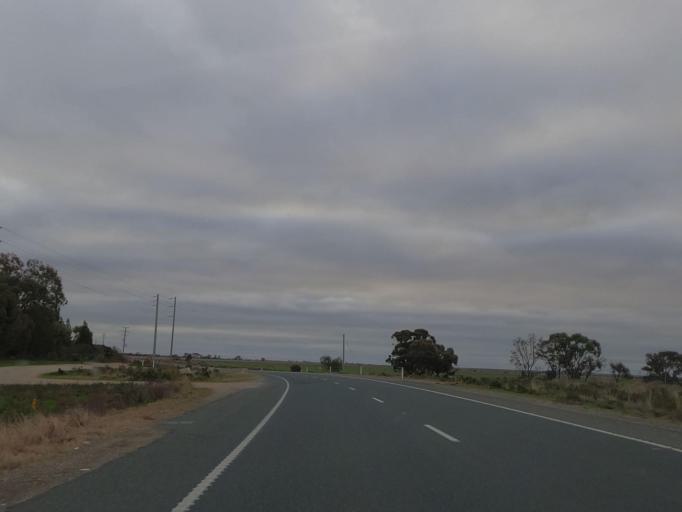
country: AU
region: Victoria
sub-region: Swan Hill
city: Swan Hill
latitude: -35.5560
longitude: 143.7774
